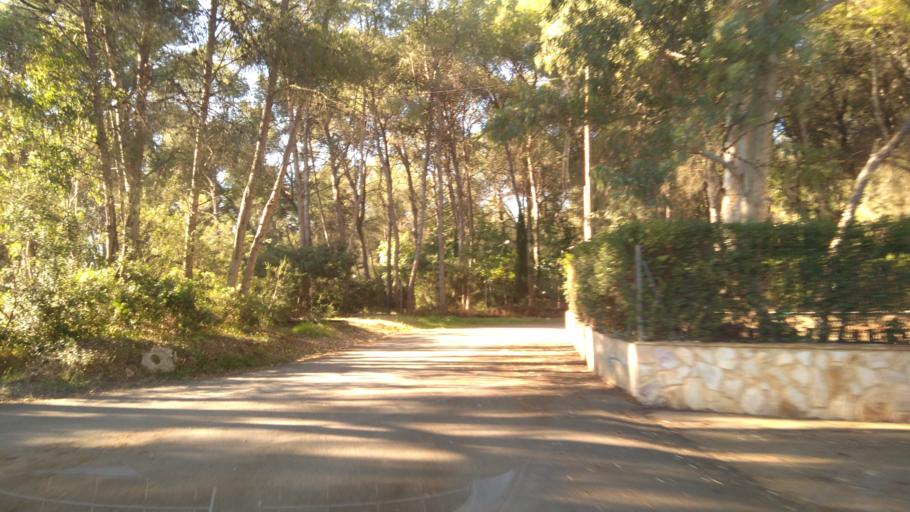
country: ES
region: Valencia
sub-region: Provincia de Valencia
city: Benimodo
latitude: 39.1778
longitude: -0.5585
